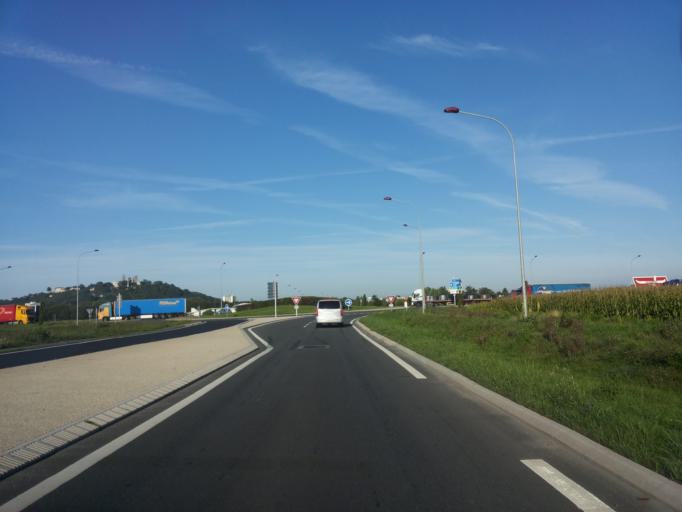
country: FR
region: Picardie
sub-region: Departement de l'Aisne
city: Athies-sous-Laon
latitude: 49.5666
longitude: 3.6620
